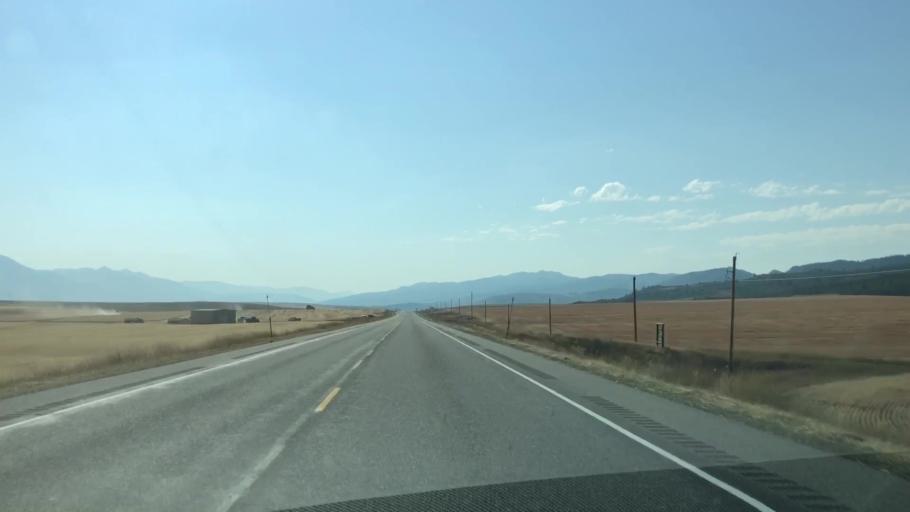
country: US
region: Idaho
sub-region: Teton County
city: Victor
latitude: 43.5078
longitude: -111.4749
